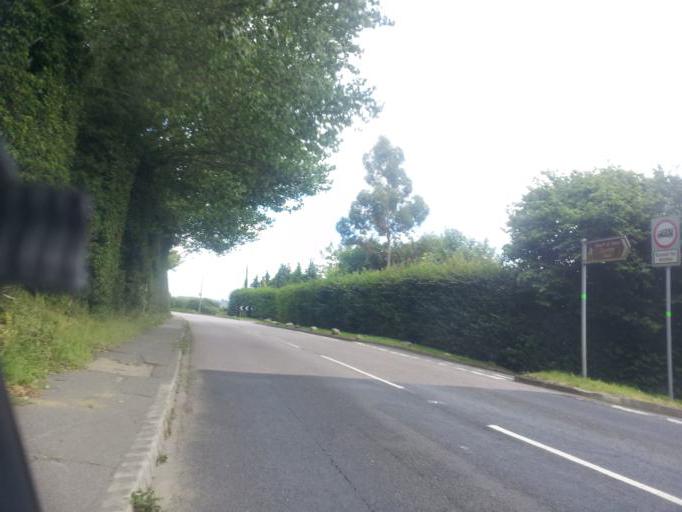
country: GB
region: England
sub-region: Kent
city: Kings Hill
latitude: 51.2562
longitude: 0.4001
